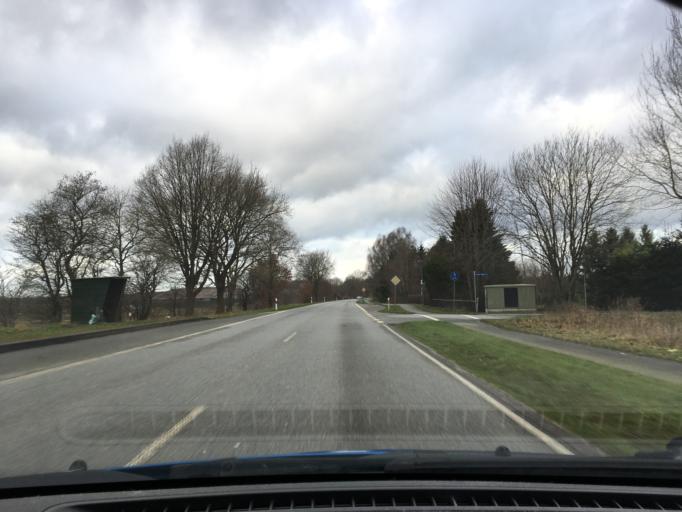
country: DE
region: Schleswig-Holstein
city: Ottenbuttel
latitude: 53.9902
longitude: 9.4929
